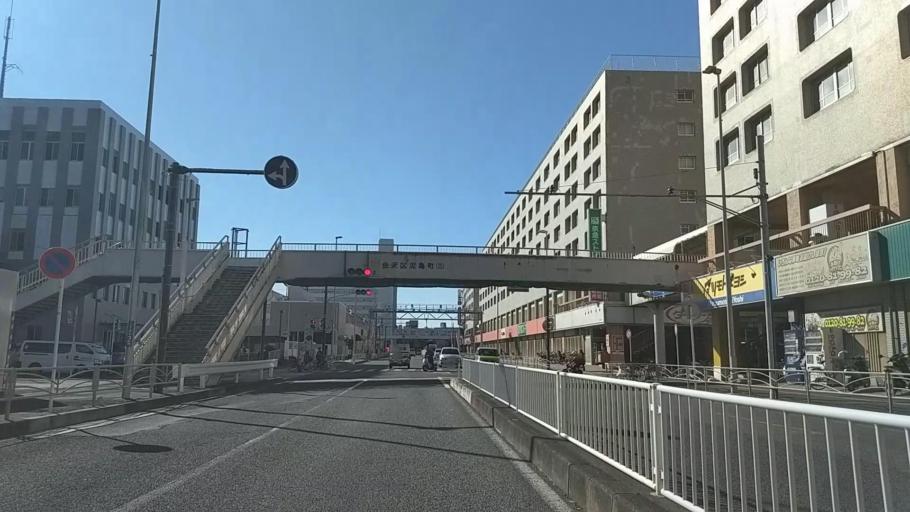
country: JP
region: Kanagawa
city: Zushi
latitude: 35.3374
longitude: 139.6239
